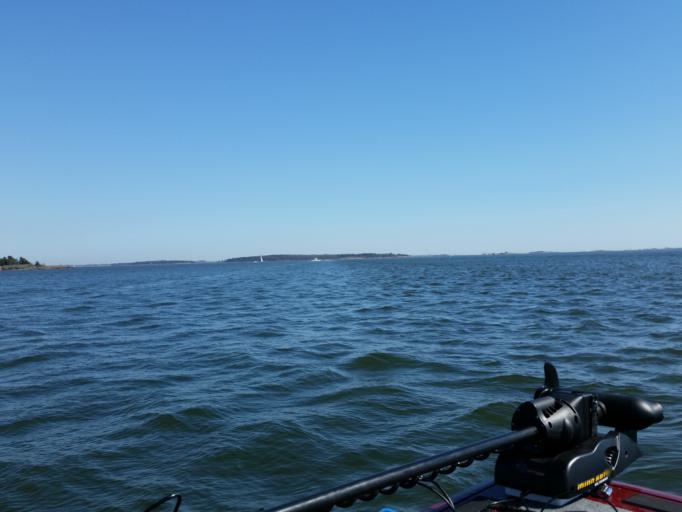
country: FI
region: Uusimaa
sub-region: Helsinki
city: Otaniemi
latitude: 60.1388
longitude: 24.8191
